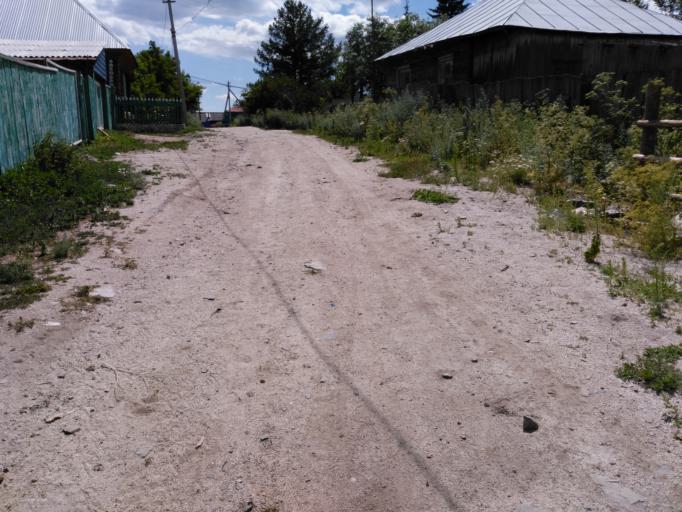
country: RU
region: Bashkortostan
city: Akhunovo
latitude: 54.2084
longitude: 59.5995
